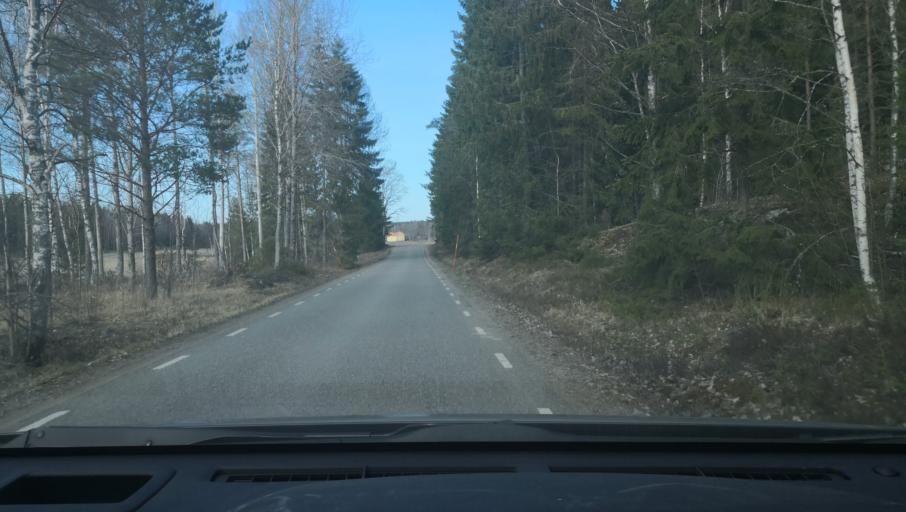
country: SE
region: Uppsala
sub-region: Heby Kommun
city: Heby
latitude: 59.8970
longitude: 16.8008
